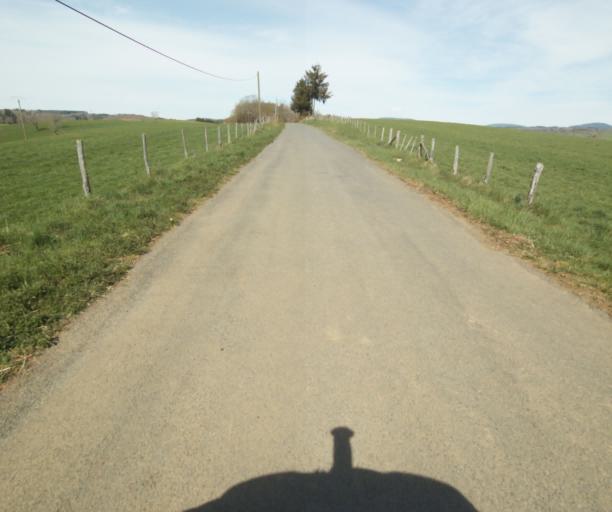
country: FR
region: Limousin
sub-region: Departement de la Correze
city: Naves
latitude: 45.3739
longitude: 1.7774
